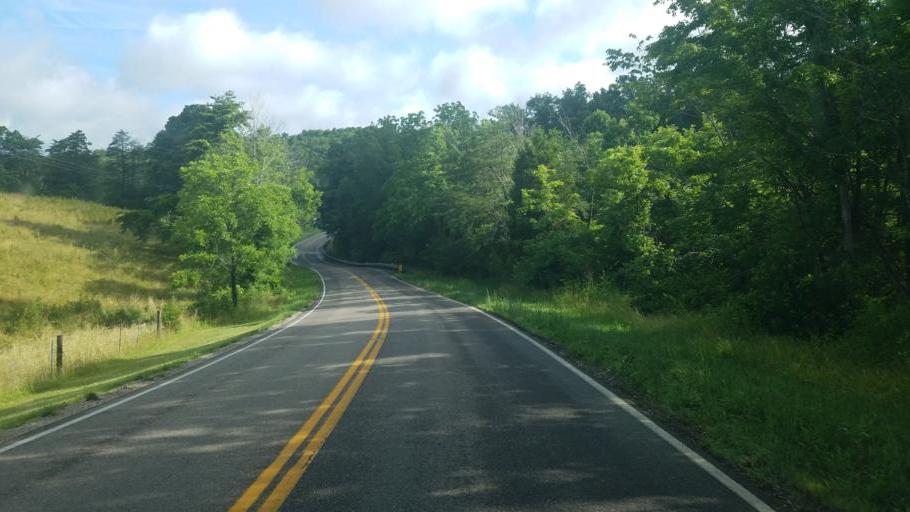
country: US
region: Ohio
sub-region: Jackson County
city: Oak Hill
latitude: 38.8389
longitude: -82.3924
